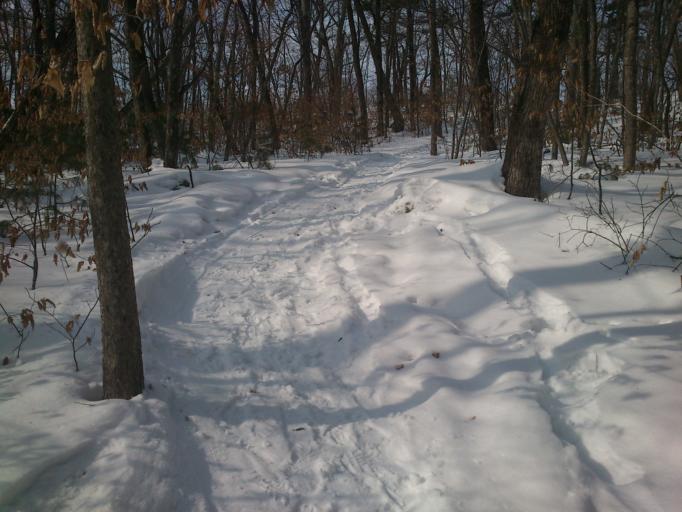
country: RU
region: Primorskiy
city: Volchanets
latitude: 43.1578
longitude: 132.7152
